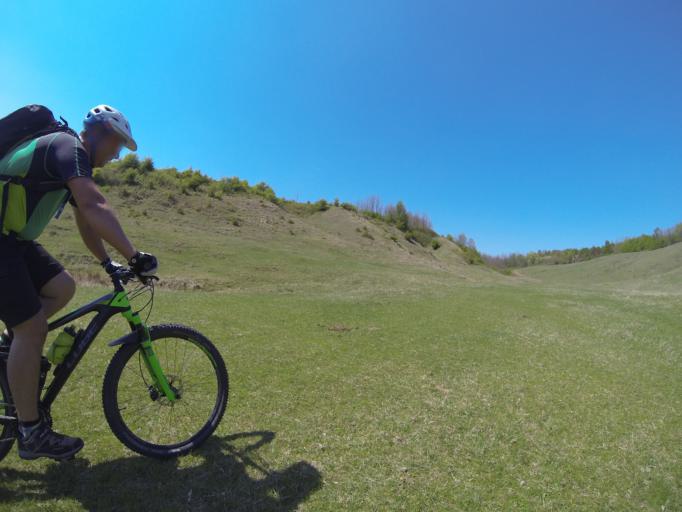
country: RO
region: Gorj
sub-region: Comuna Crusetu
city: Crusetu
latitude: 44.5847
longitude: 23.6604
